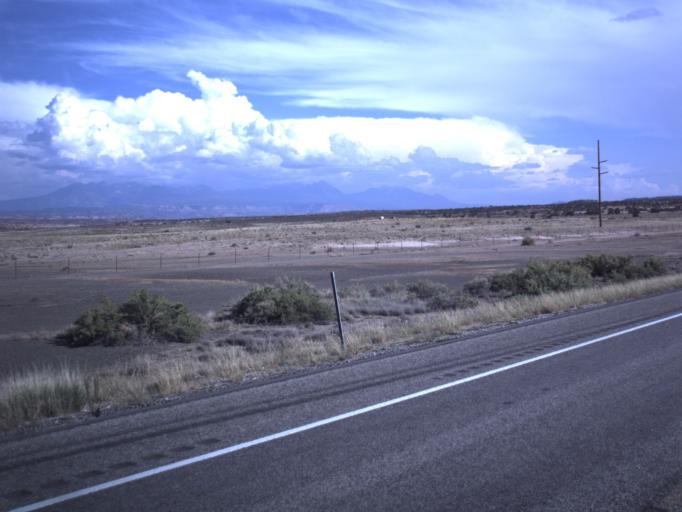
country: US
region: Utah
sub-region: Grand County
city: Moab
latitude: 38.7047
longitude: -109.7014
